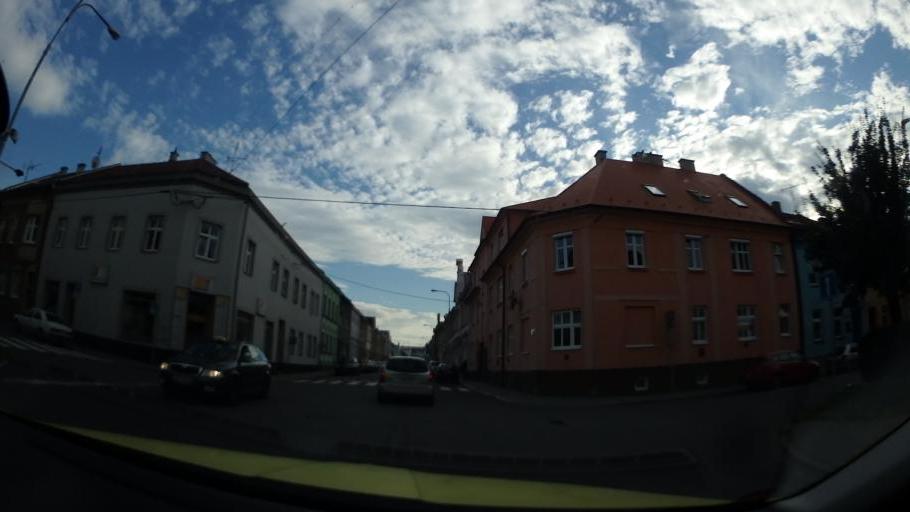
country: CZ
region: Moravskoslezsky
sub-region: Okres Novy Jicin
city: Novy Jicin
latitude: 49.5980
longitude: 18.0150
